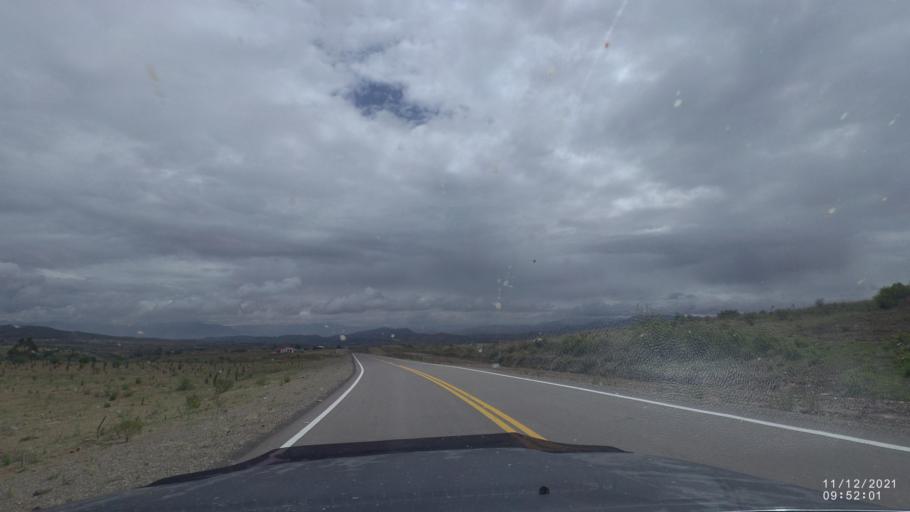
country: BO
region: Cochabamba
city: Tarata
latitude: -17.7936
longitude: -65.9496
